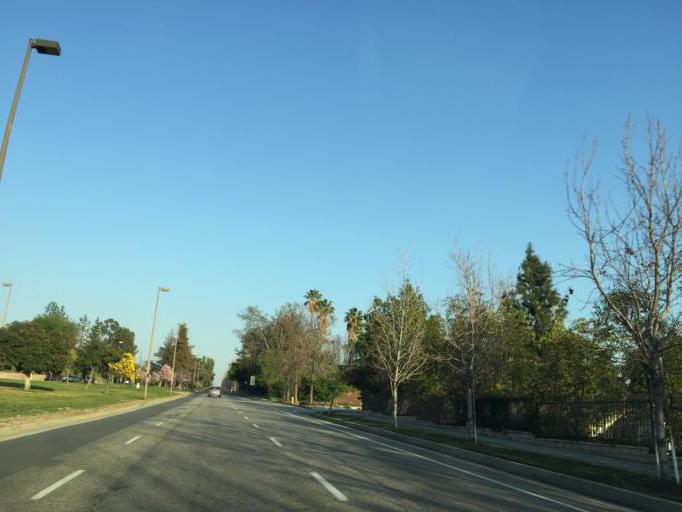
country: US
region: California
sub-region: Los Angeles County
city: East Pasadena
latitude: 34.1615
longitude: -118.0799
